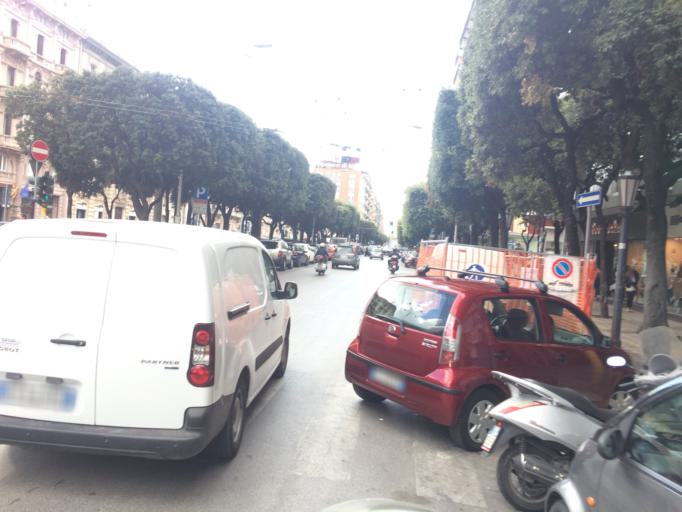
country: IT
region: Apulia
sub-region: Provincia di Bari
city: Bari
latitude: 41.1233
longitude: 16.8722
